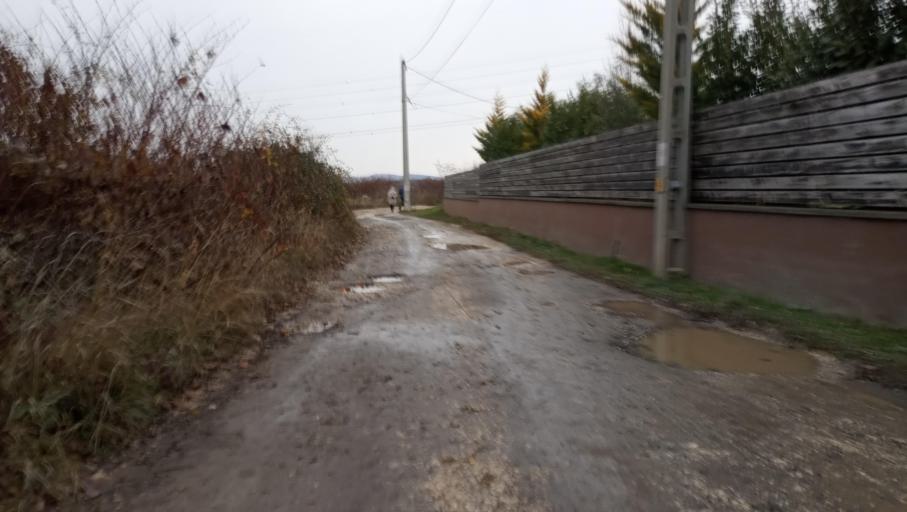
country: HU
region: Pest
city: Urom
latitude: 47.5979
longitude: 19.0295
